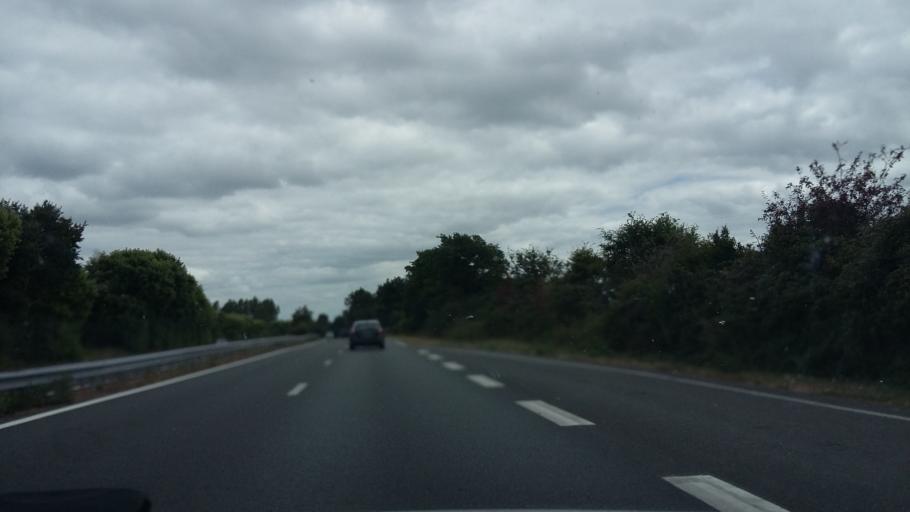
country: FR
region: Pays de la Loire
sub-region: Departement de la Vendee
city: Venansault
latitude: 46.6956
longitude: -1.4819
